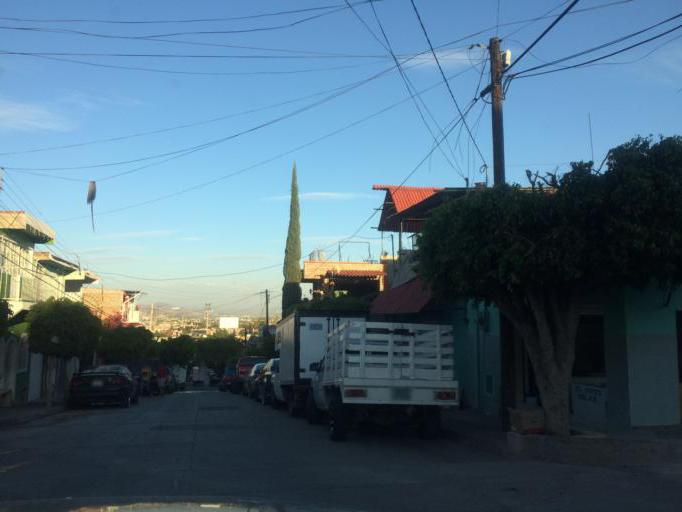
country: MX
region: Guanajuato
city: Leon
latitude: 21.1352
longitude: -101.7016
